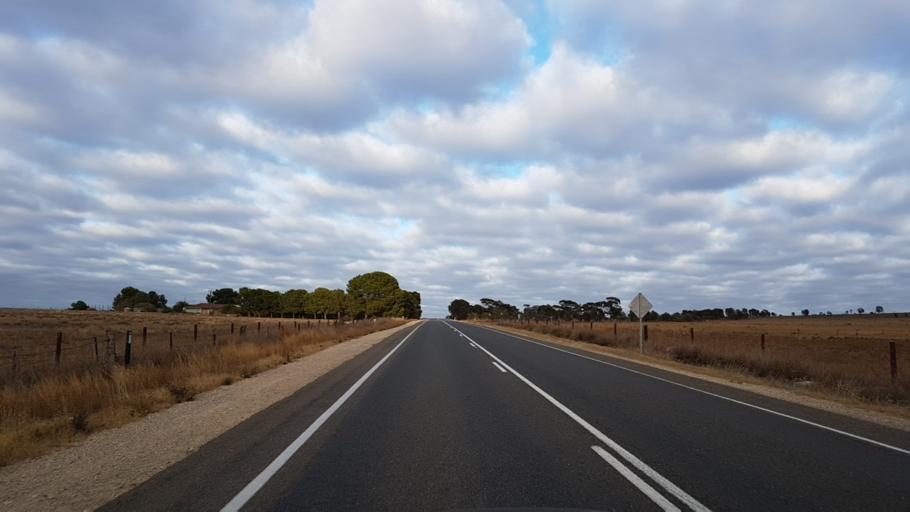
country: AU
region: South Australia
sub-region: Mount Barker
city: Callington
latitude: -35.1842
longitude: 139.0015
